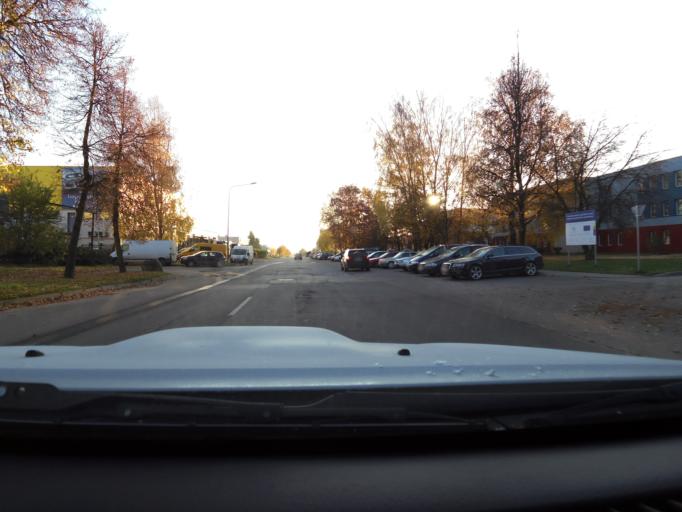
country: LT
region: Vilnius County
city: Vilkpede
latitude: 54.6310
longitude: 25.2573
